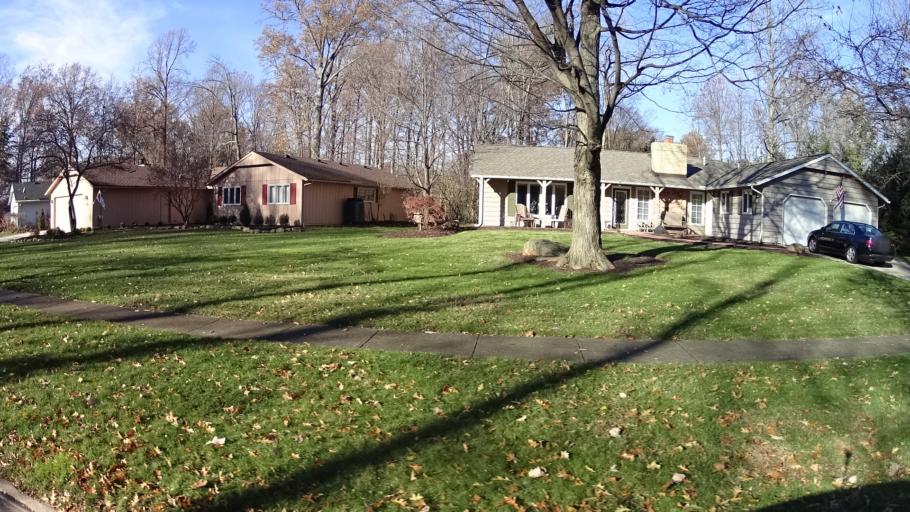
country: US
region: Ohio
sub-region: Lorain County
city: North Ridgeville
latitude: 41.4031
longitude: -81.9748
